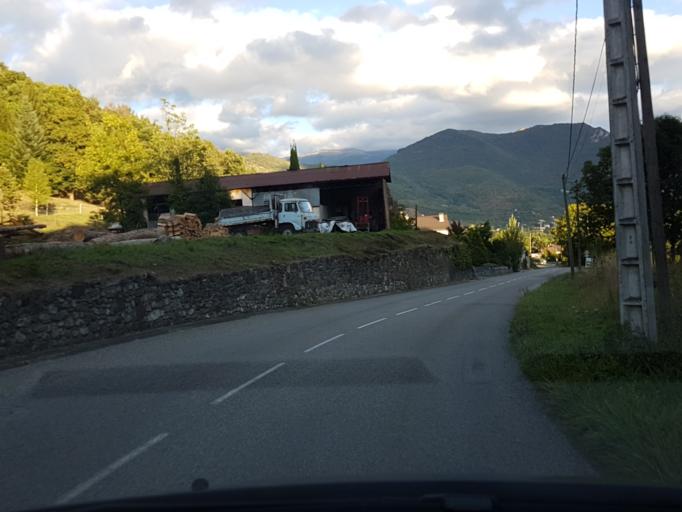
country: FR
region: Midi-Pyrenees
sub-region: Departement de l'Ariege
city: Tarascon-sur-Ariege
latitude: 42.8586
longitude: 1.5802
